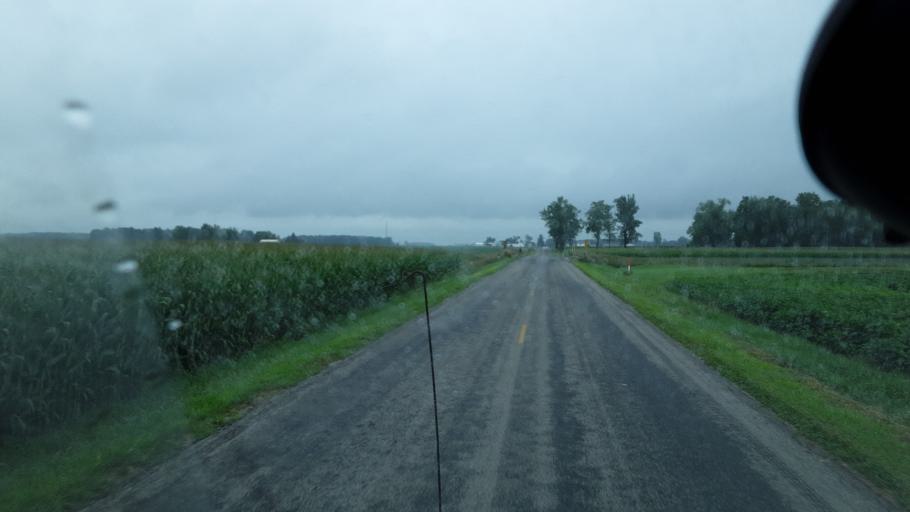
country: US
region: Indiana
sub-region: Wells County
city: Ossian
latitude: 40.8503
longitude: -85.1092
